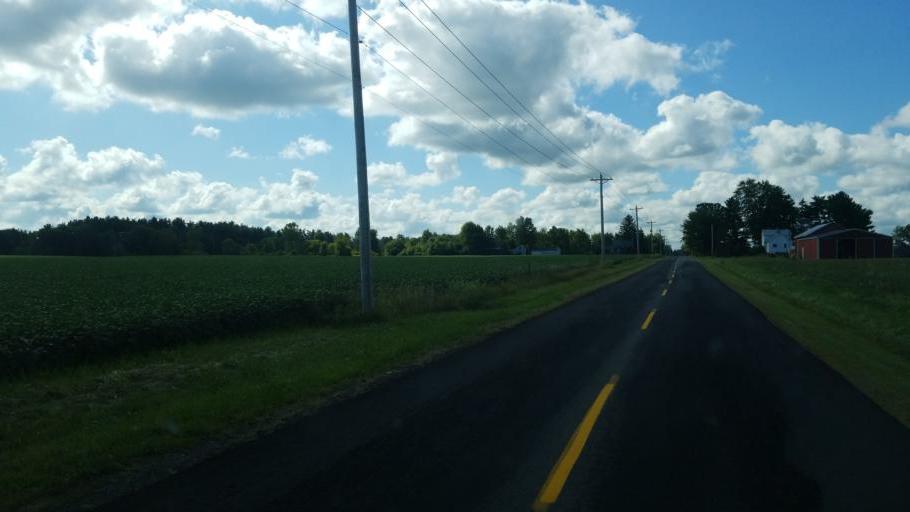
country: US
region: Ohio
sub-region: Lorain County
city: Lagrange
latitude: 41.2327
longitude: -82.1805
